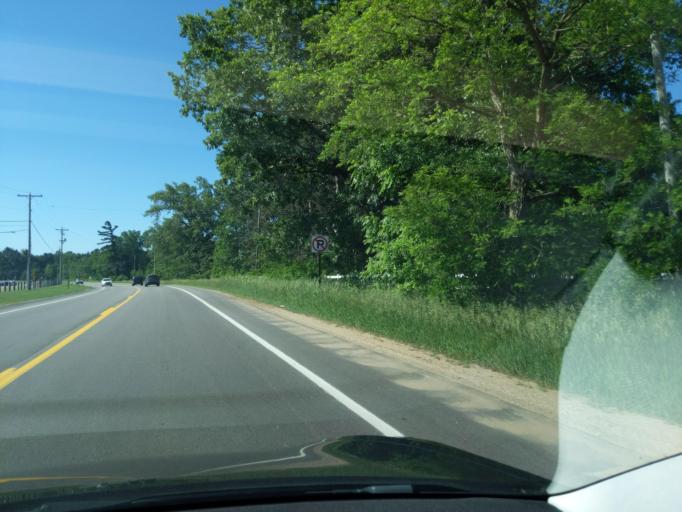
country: US
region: Michigan
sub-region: Muskegon County
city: Lakewood Club
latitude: 43.3442
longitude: -86.2819
